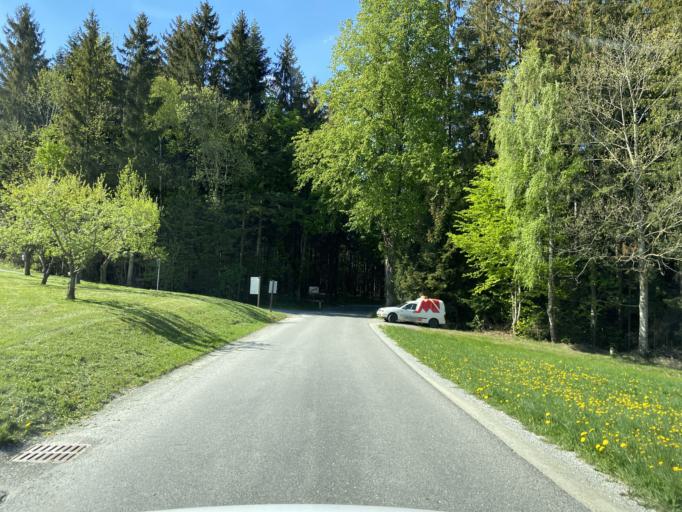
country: AT
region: Styria
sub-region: Politischer Bezirk Weiz
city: Strallegg
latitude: 47.3678
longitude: 15.7125
